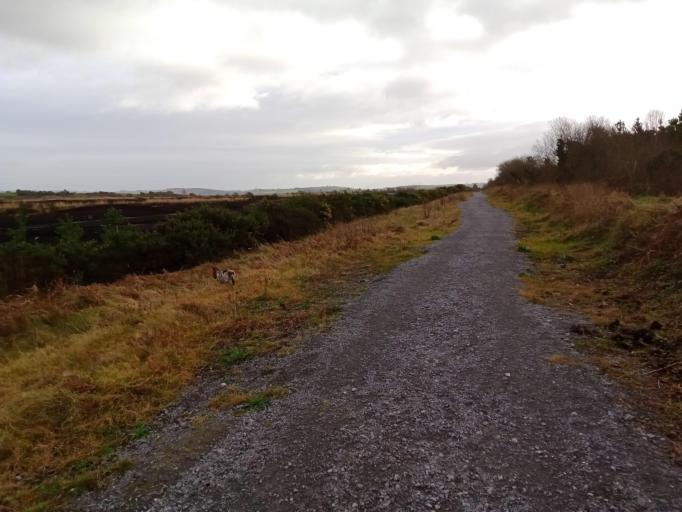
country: IE
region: Munster
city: Thurles
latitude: 52.5987
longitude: -7.7483
